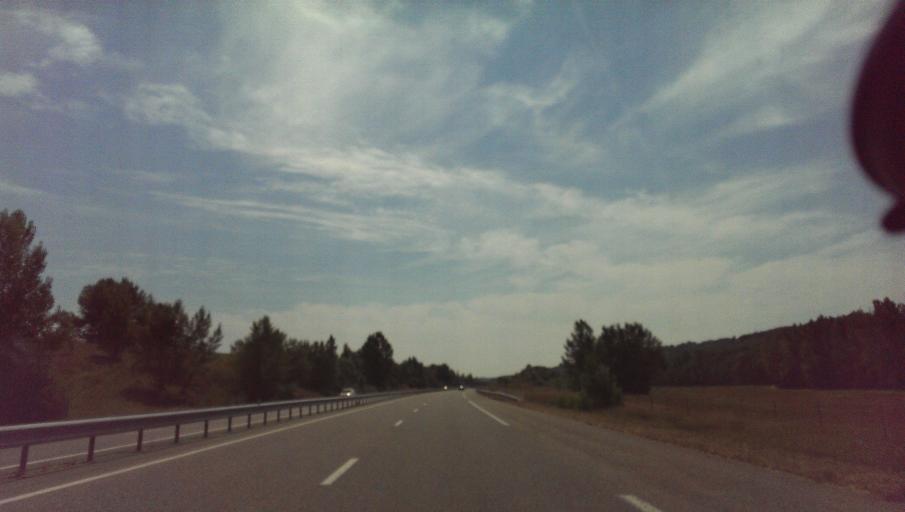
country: FR
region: Midi-Pyrenees
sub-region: Departement de la Haute-Garonne
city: Calmont
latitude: 43.3156
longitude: 1.6457
